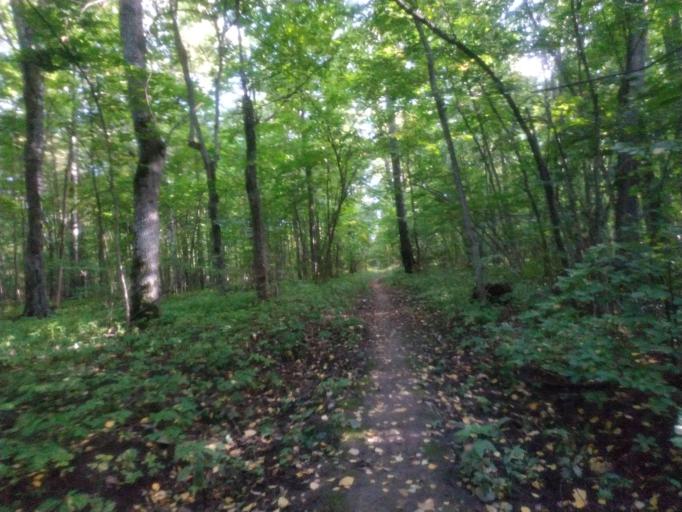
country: RU
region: Chuvashia
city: Novyye Lapsary
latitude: 56.1363
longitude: 47.1102
